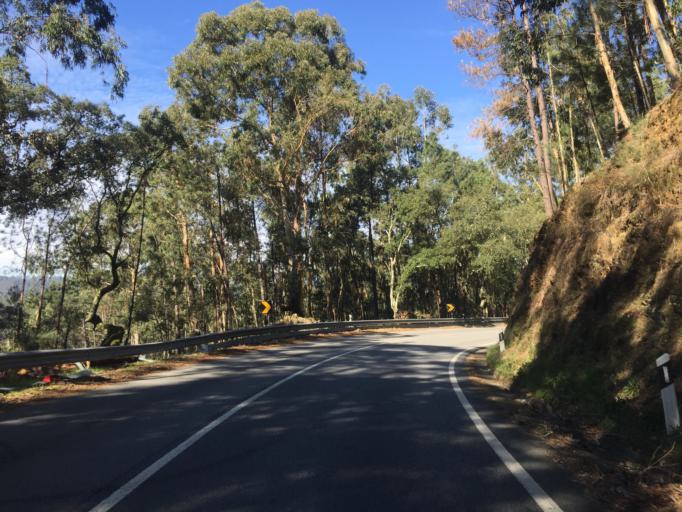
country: PT
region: Aveiro
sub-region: Vale de Cambra
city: Macieira de Cambra
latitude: 40.8990
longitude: -8.3315
